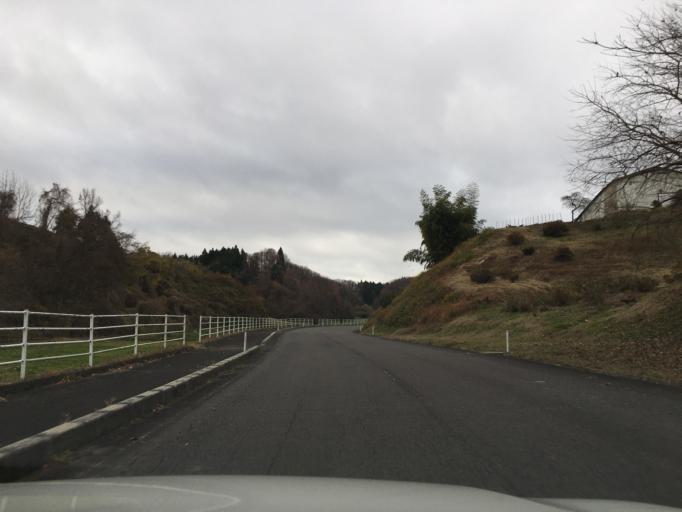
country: JP
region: Fukushima
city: Funehikimachi-funehiki
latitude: 37.4718
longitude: 140.5474
